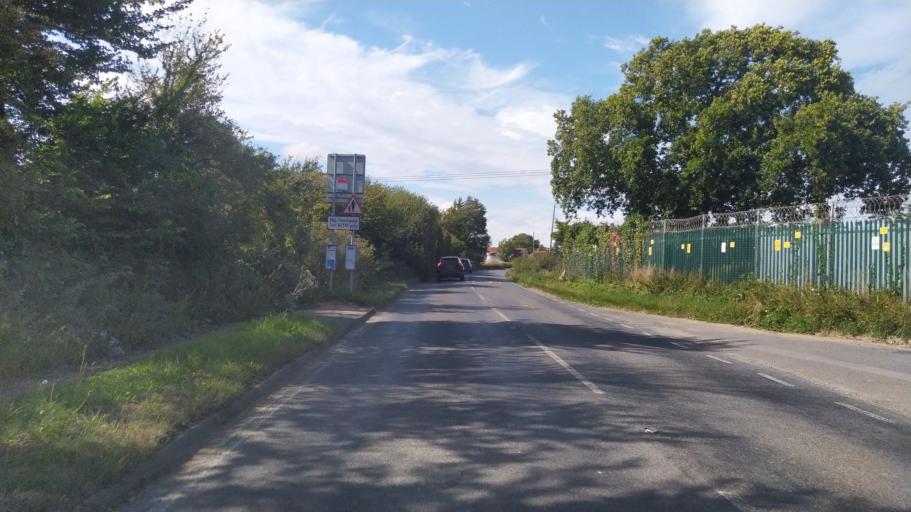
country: GB
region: England
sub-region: West Sussex
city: Chichester
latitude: 50.8167
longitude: -0.7680
